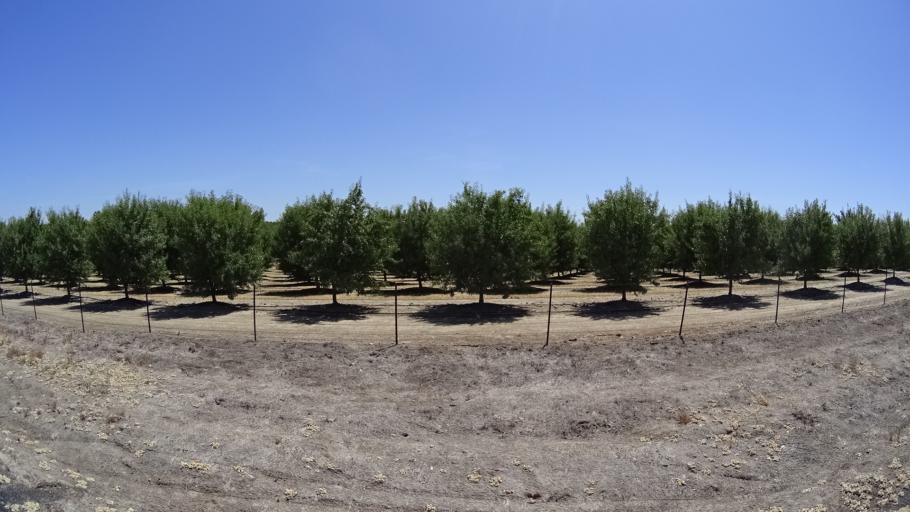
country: US
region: California
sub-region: Calaveras County
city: Rancho Calaveras
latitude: 38.0971
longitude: -120.9449
